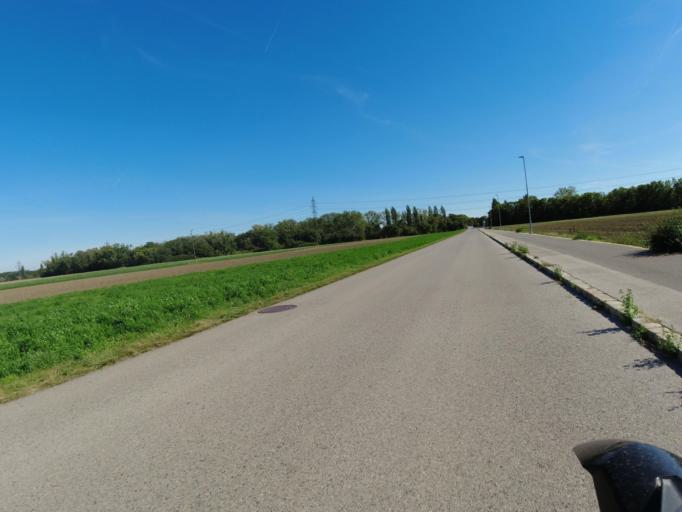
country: AT
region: Lower Austria
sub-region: Politischer Bezirk Baden
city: Traiskirchen
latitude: 48.0222
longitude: 16.3113
